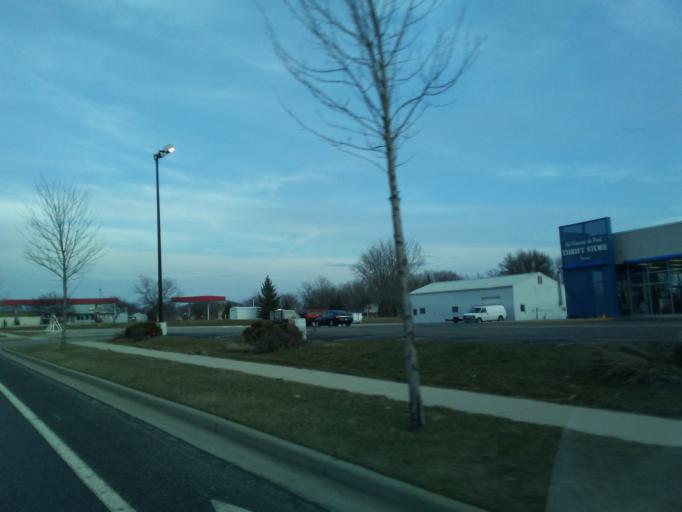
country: US
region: Wisconsin
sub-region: Dane County
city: Verona
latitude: 42.9885
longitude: -89.5447
